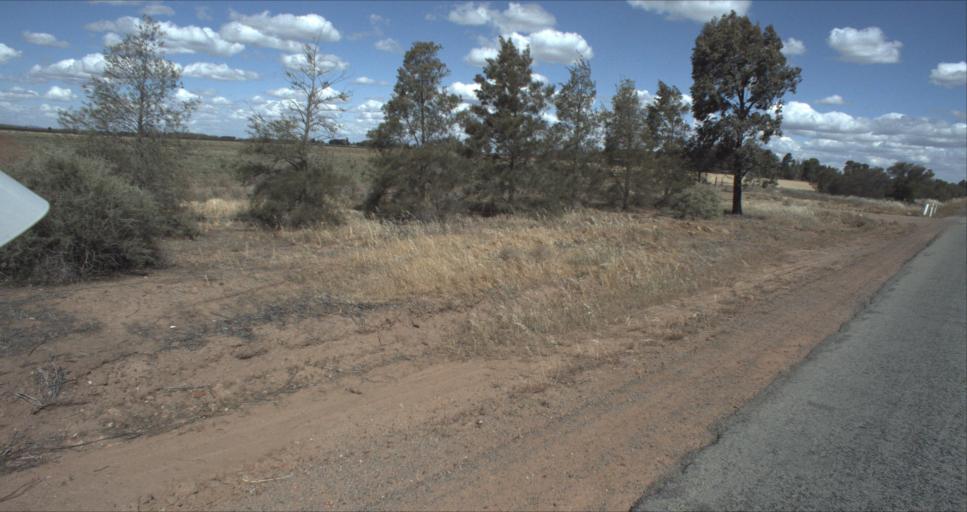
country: AU
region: New South Wales
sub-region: Leeton
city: Leeton
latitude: -34.4770
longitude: 146.2498
